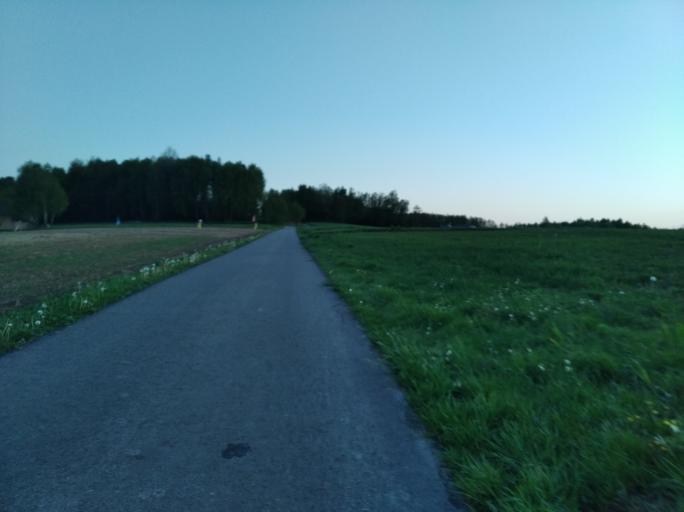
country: PL
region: Subcarpathian Voivodeship
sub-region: Powiat strzyzowski
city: Czudec
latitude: 49.9167
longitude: 21.8064
